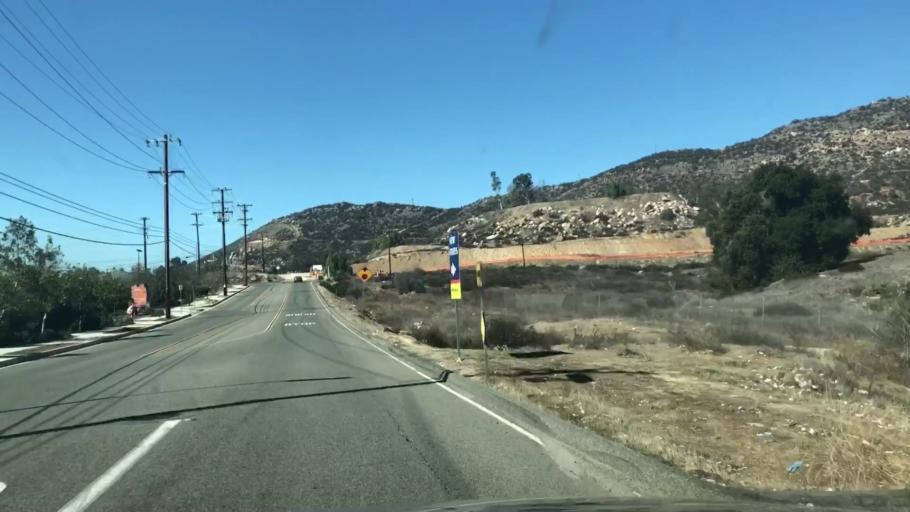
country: US
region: California
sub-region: Riverside County
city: Murrieta Hot Springs
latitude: 33.6051
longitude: -117.1736
